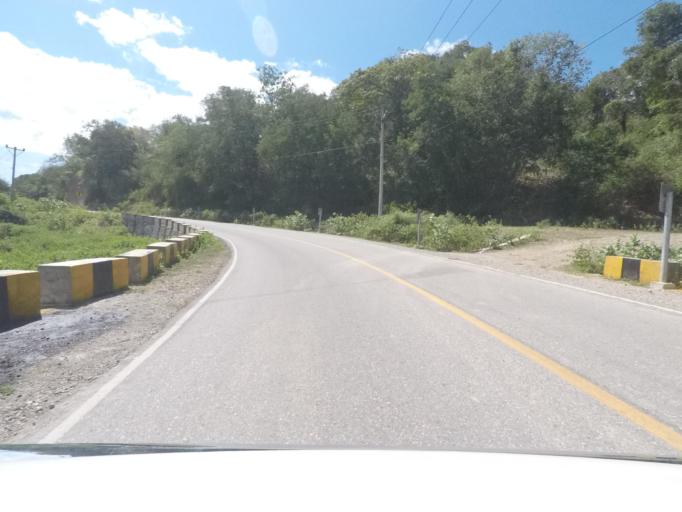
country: TL
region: Lautem
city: Lospalos
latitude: -8.3759
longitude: 126.8923
